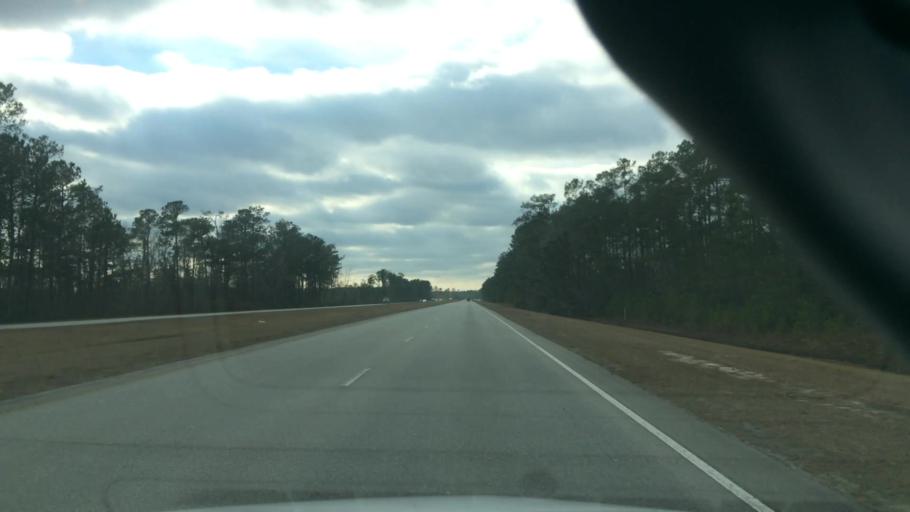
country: US
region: North Carolina
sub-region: Brunswick County
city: Bolivia
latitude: 34.0591
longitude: -78.2064
